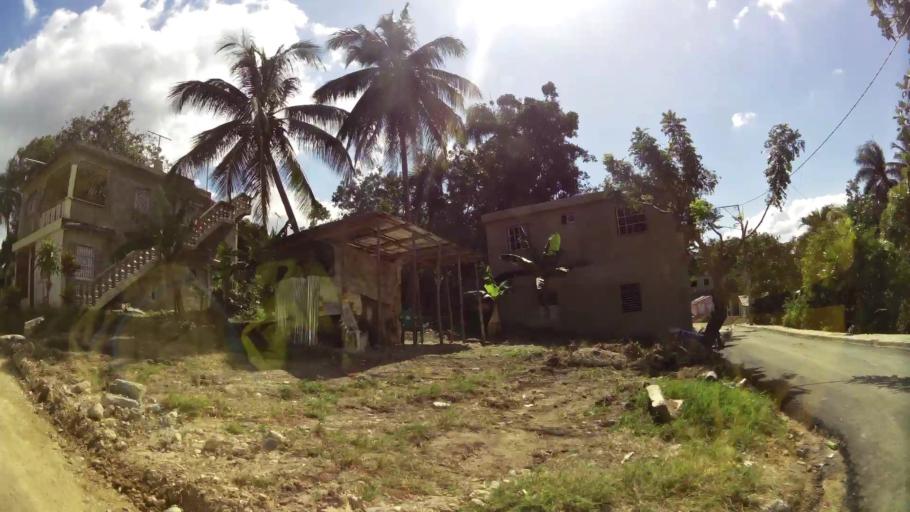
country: DO
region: San Cristobal
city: San Cristobal
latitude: 18.4252
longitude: -70.0807
